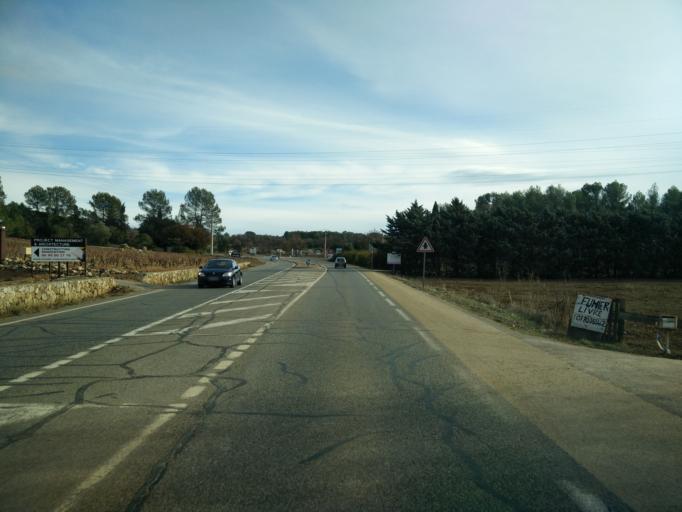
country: FR
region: Provence-Alpes-Cote d'Azur
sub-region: Departement du Var
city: Lorgues
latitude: 43.4678
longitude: 6.3859
